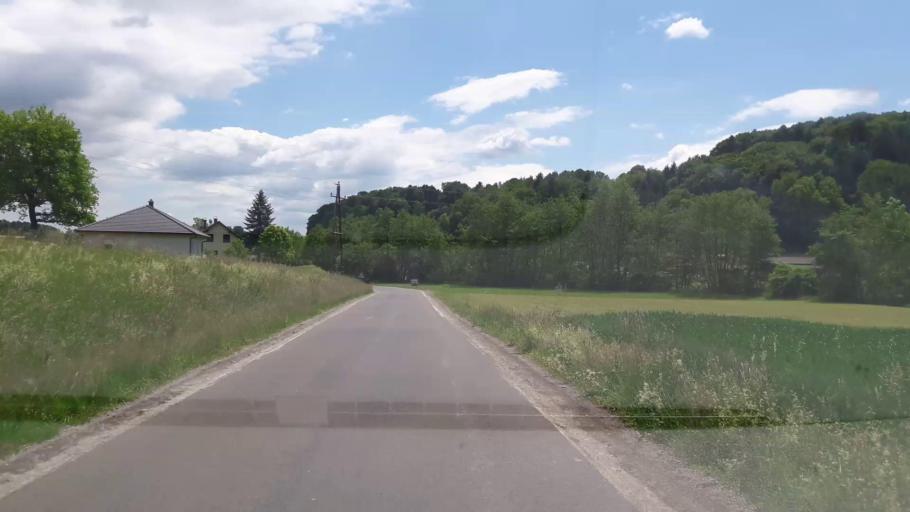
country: AT
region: Styria
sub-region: Politischer Bezirk Suedoststeiermark
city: Unterlamm
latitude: 46.9881
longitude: 16.0441
